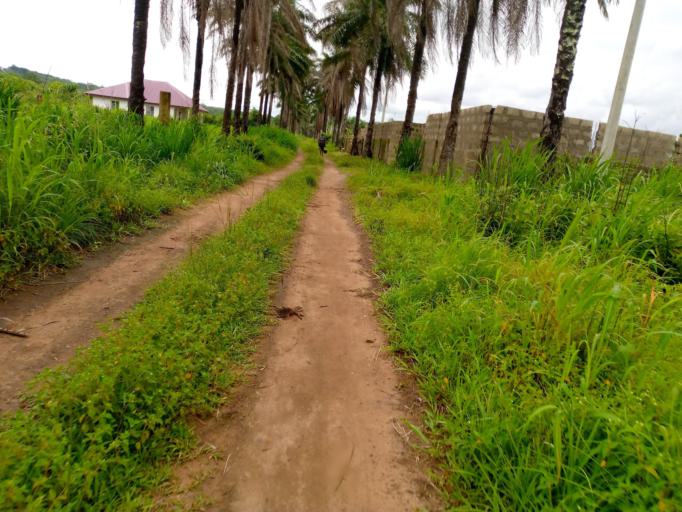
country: SL
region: Southern Province
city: Moyamba
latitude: 8.1482
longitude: -12.4416
